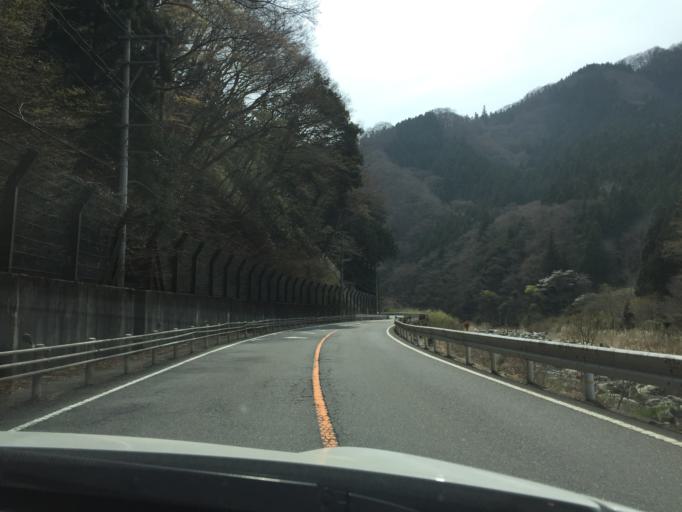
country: JP
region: Fukushima
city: Ishikawa
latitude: 37.0478
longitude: 140.6175
